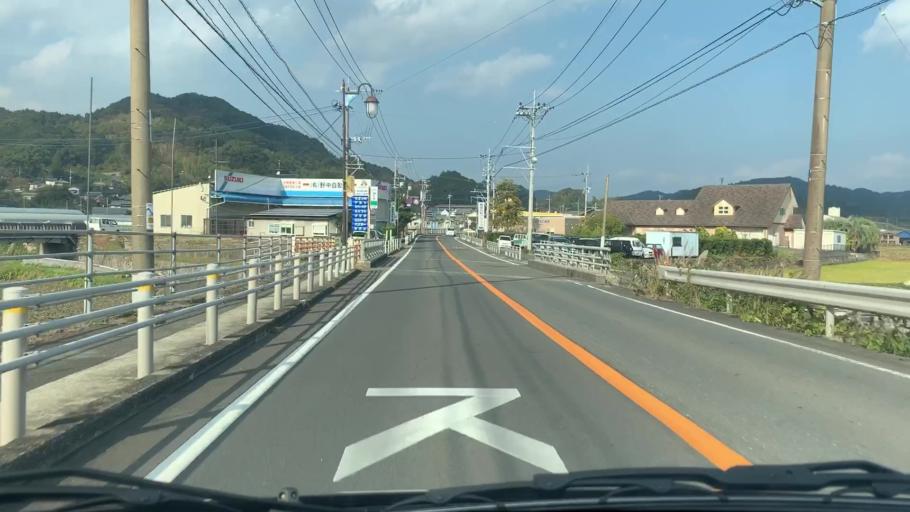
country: JP
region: Nagasaki
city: Togitsu
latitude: 32.9436
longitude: 129.7821
